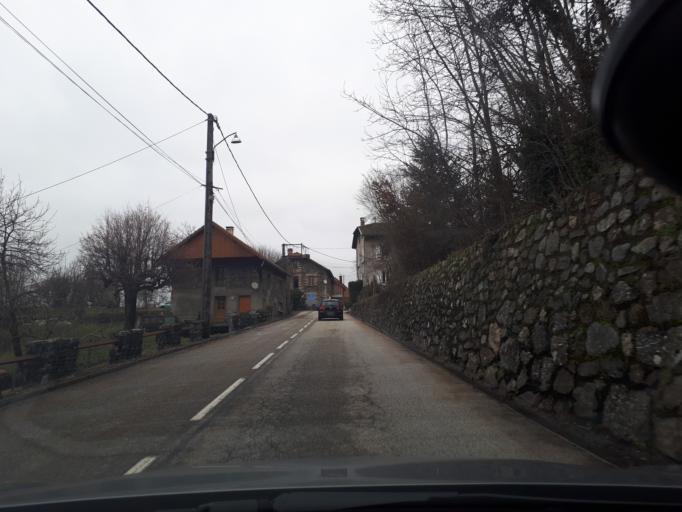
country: FR
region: Rhone-Alpes
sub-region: Departement de l'Isere
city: Vaulnaveys-le-Bas
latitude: 45.1143
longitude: 5.8306
